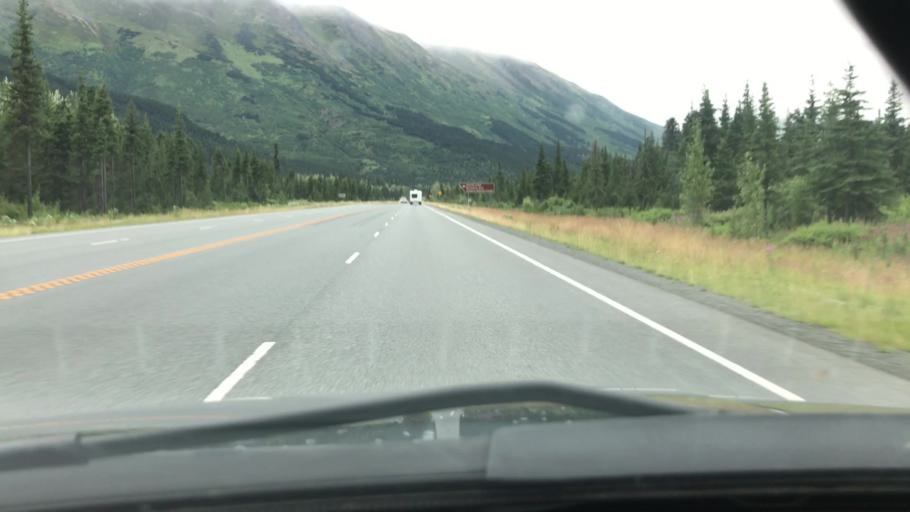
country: US
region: Alaska
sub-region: Anchorage Municipality
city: Girdwood
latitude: 60.7287
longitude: -149.3152
